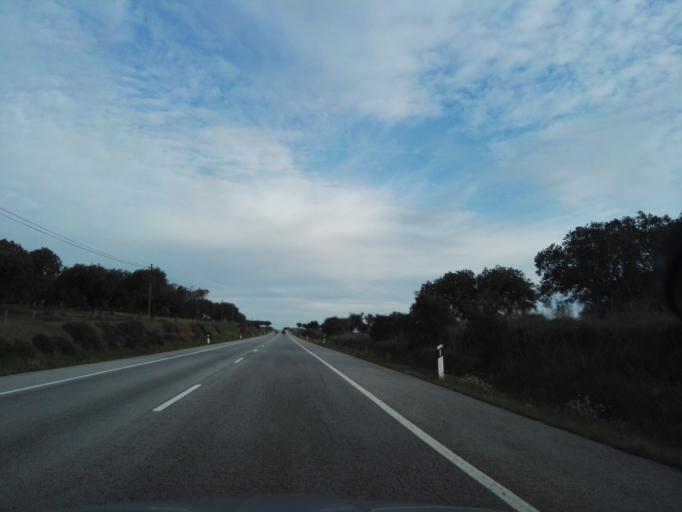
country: PT
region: Portalegre
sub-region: Arronches
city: Arronches
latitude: 39.1564
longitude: -7.3169
